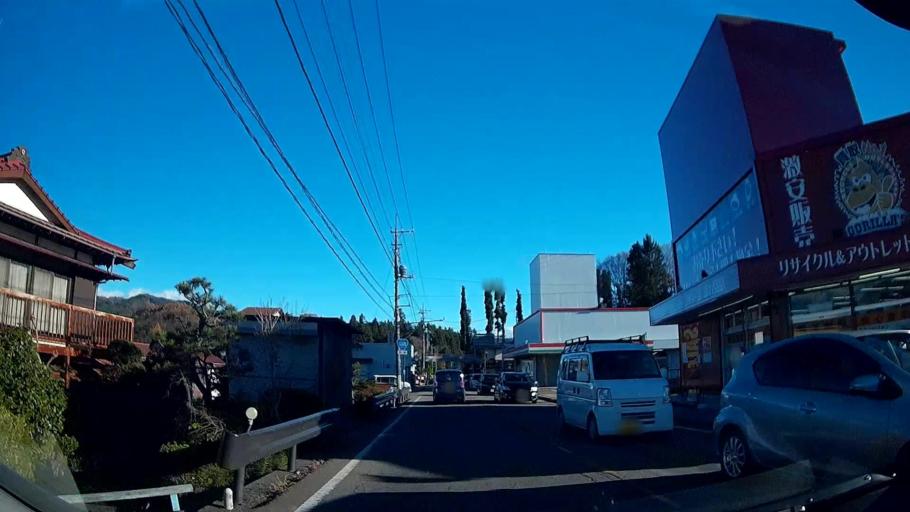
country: JP
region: Yamanashi
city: Fujikawaguchiko
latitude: 35.4713
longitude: 138.7981
